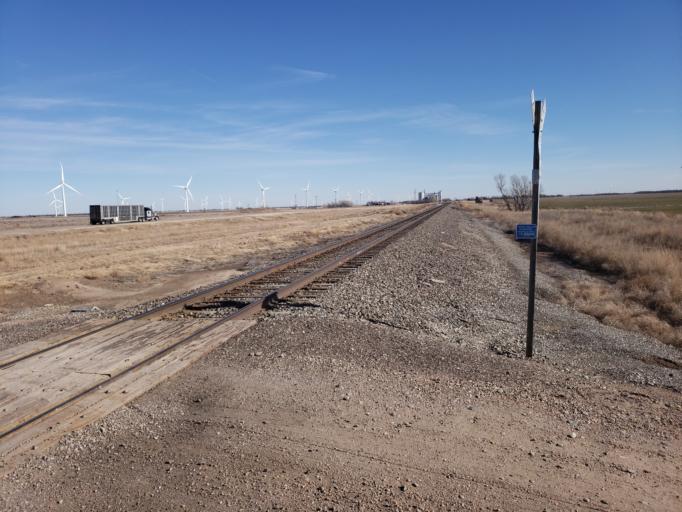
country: US
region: Kansas
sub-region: Edwards County
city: Kinsley
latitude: 37.8683
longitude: -99.6800
